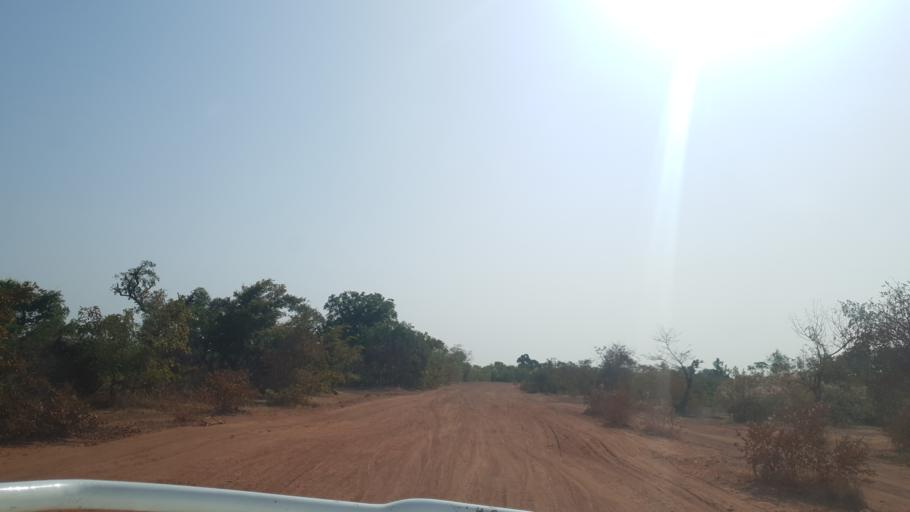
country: ML
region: Koulikoro
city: Dioila
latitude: 12.6711
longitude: -6.7047
